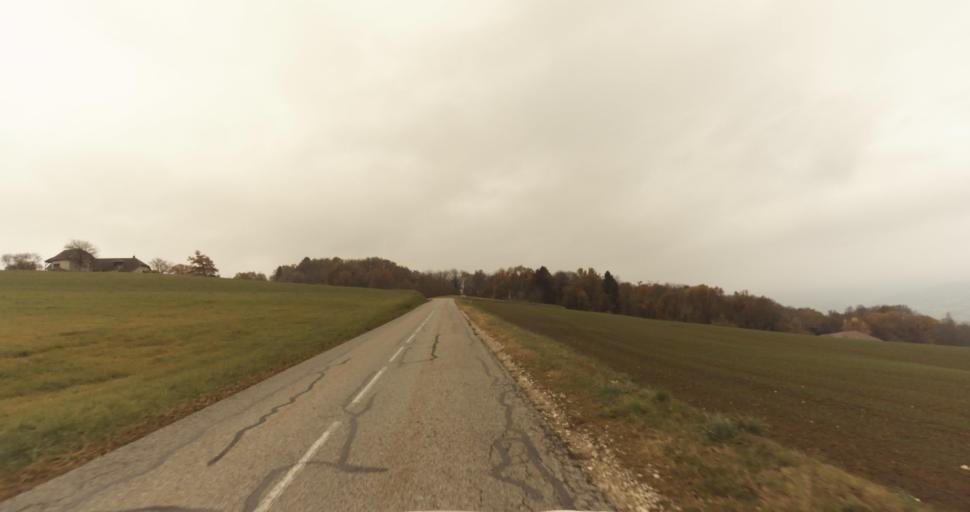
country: FR
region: Rhone-Alpes
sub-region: Departement de la Haute-Savoie
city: Alby-sur-Cheran
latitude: 45.8054
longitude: 5.9958
